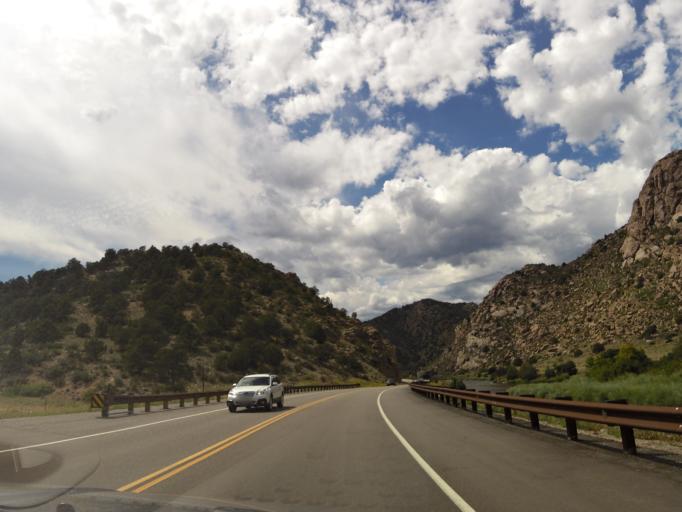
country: US
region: Colorado
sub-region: Custer County
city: Westcliffe
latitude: 38.3903
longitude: -105.6448
